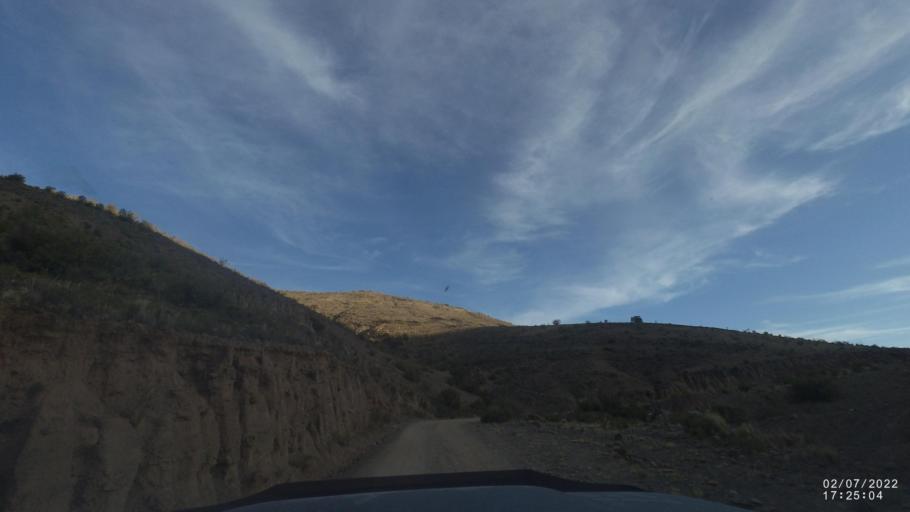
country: BO
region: Cochabamba
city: Irpa Irpa
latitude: -17.8752
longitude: -66.6062
